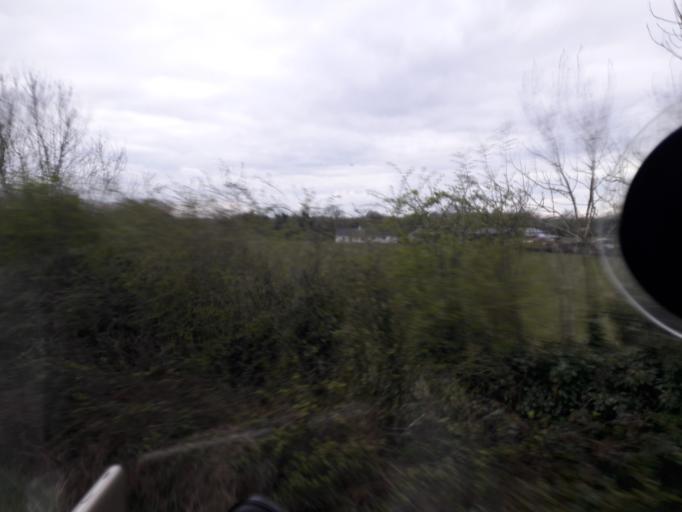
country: IE
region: Leinster
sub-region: An Longfort
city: Edgeworthstown
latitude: 53.6905
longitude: -7.6128
